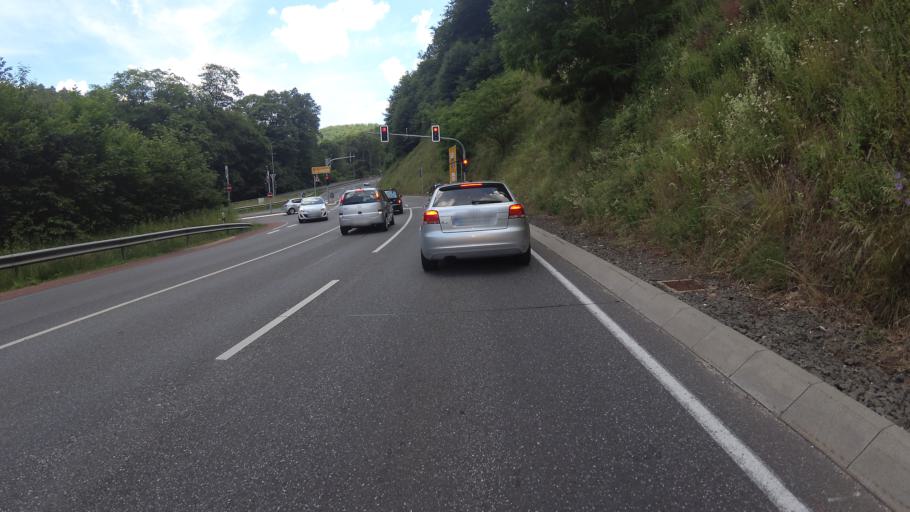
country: DE
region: Rheinland-Pfalz
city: Landstuhl
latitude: 49.4037
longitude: 7.5739
